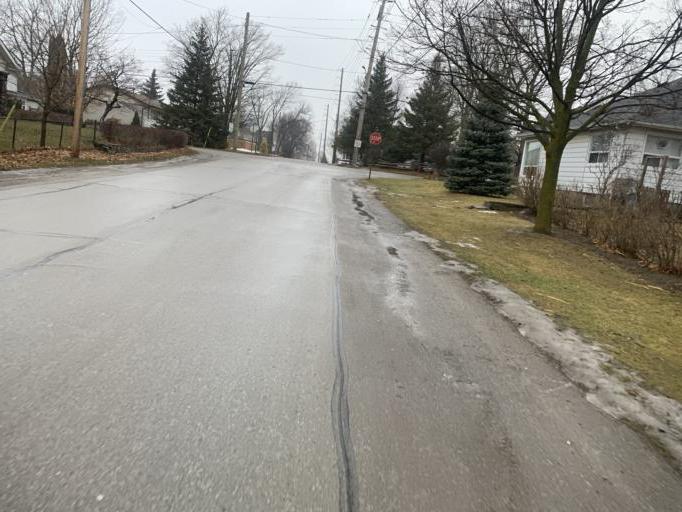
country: CA
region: Ontario
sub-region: Halton
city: Milton
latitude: 43.6567
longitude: -79.9227
